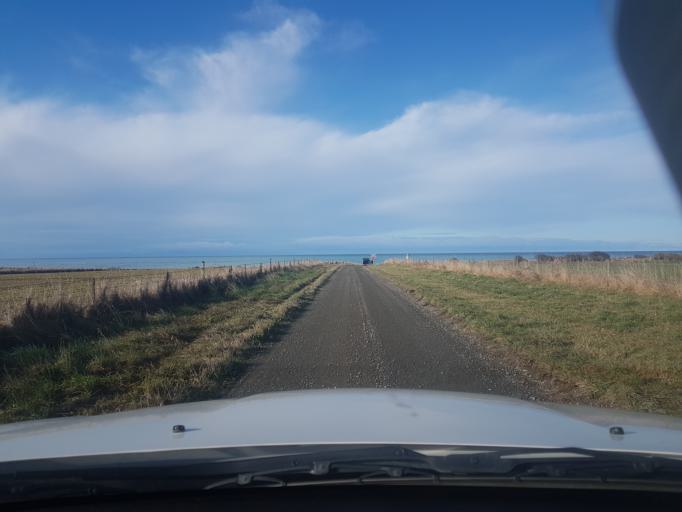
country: NZ
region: Canterbury
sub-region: Timaru District
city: Timaru
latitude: -44.4634
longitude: 171.2414
